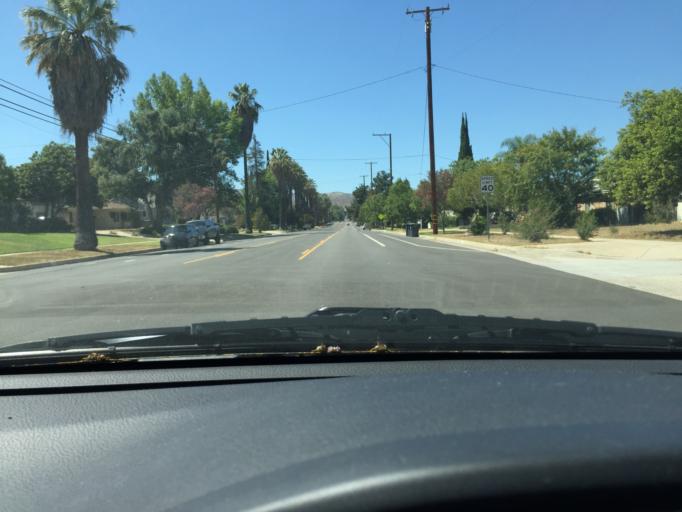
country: US
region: California
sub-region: San Bernardino County
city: Redlands
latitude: 34.0460
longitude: -117.1870
